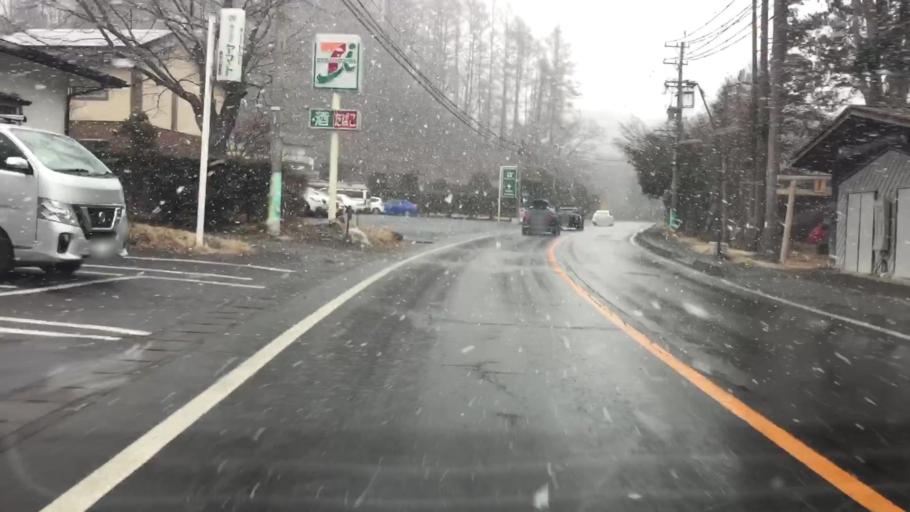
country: JP
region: Nagano
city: Komoro
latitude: 36.3556
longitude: 138.5895
